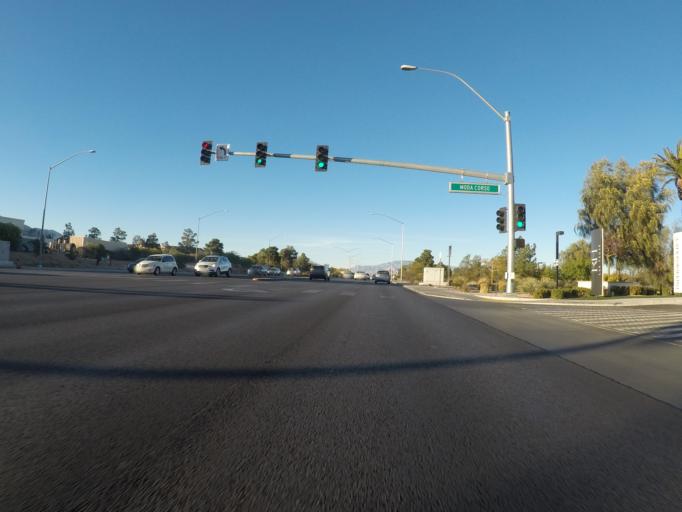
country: US
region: Nevada
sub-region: Clark County
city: Summerlin South
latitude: 36.1699
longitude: -115.2869
